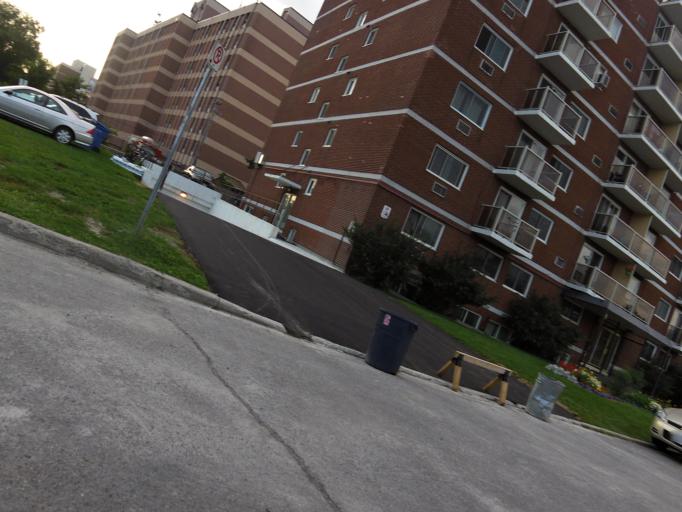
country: CA
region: Ontario
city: Bells Corners
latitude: 45.3673
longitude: -75.7755
